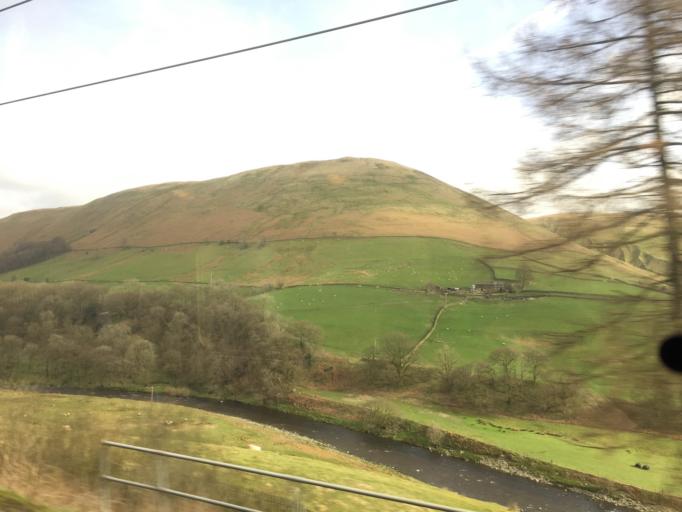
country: GB
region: England
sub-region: Cumbria
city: Sedbergh
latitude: 54.3876
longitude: -2.5866
